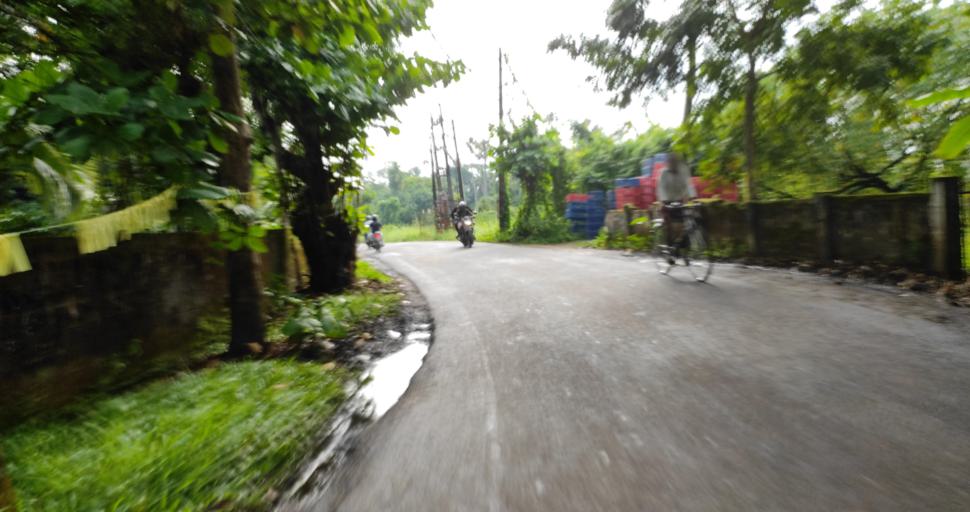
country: IN
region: Kerala
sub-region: Kottayam
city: Kottayam
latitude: 9.5782
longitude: 76.4991
